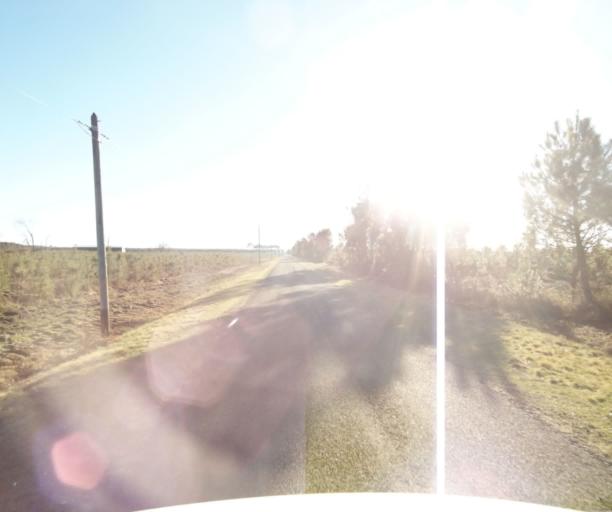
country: FR
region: Aquitaine
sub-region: Departement des Landes
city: Gabarret
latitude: 44.1315
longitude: -0.0936
